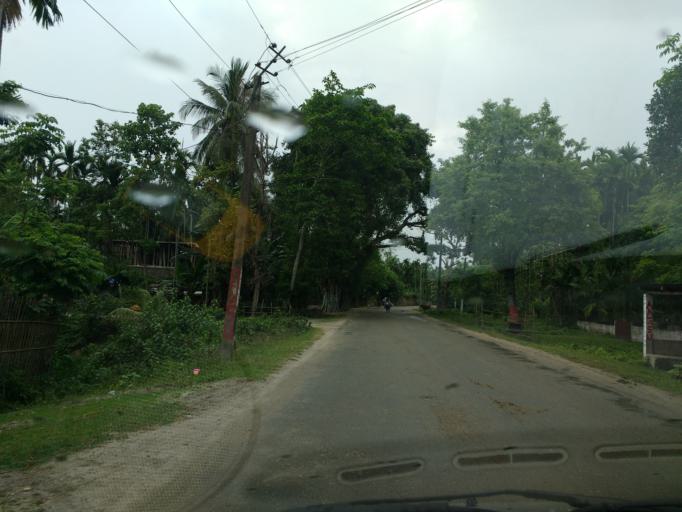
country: IN
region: Assam
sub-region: Udalguri
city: Udalguri
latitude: 26.7286
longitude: 92.2125
